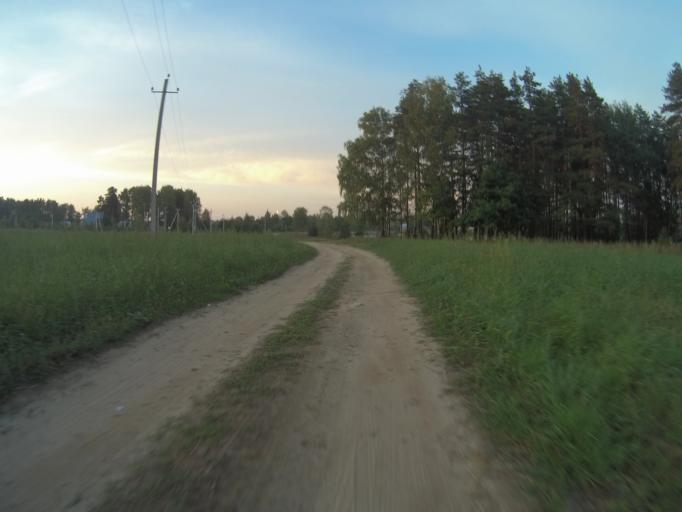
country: RU
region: Vladimir
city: Kommunar
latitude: 56.0468
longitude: 40.4776
